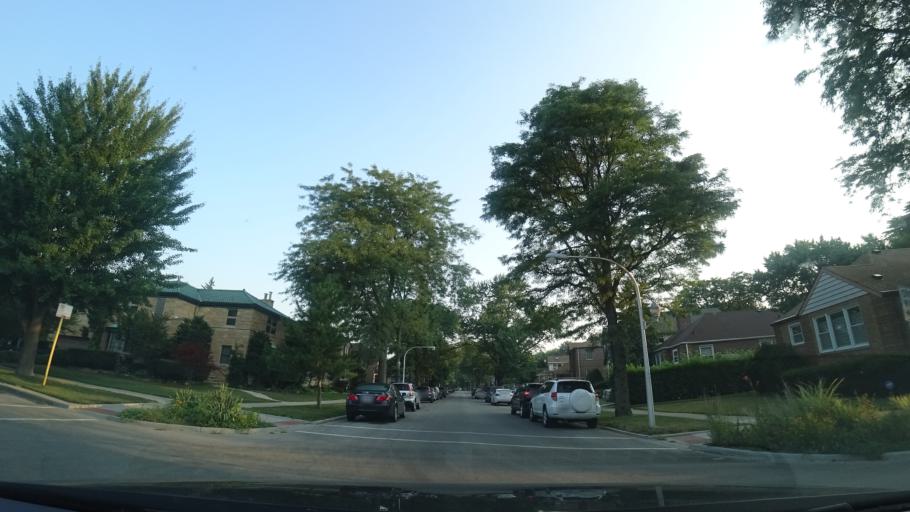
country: US
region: Illinois
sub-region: Cook County
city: Lincolnwood
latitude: 41.9794
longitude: -87.7040
